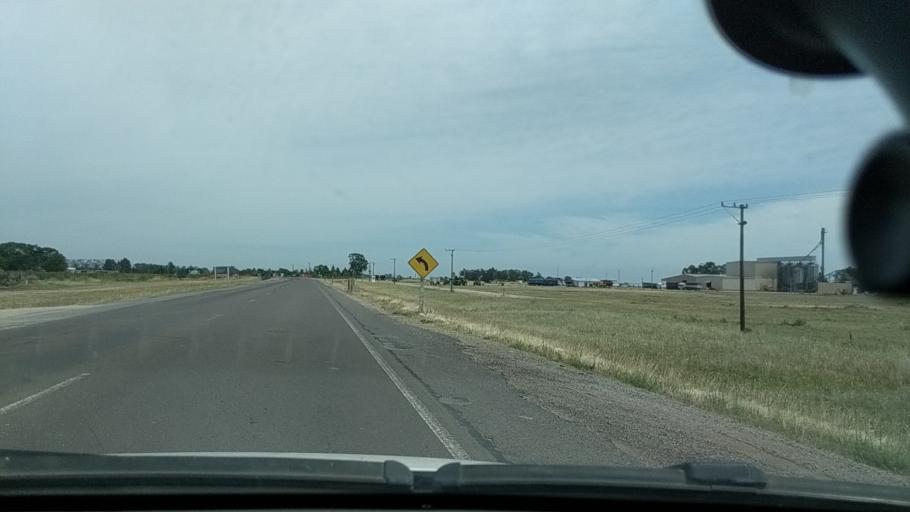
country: UY
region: Durazno
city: Durazno
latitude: -33.4459
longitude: -56.4773
